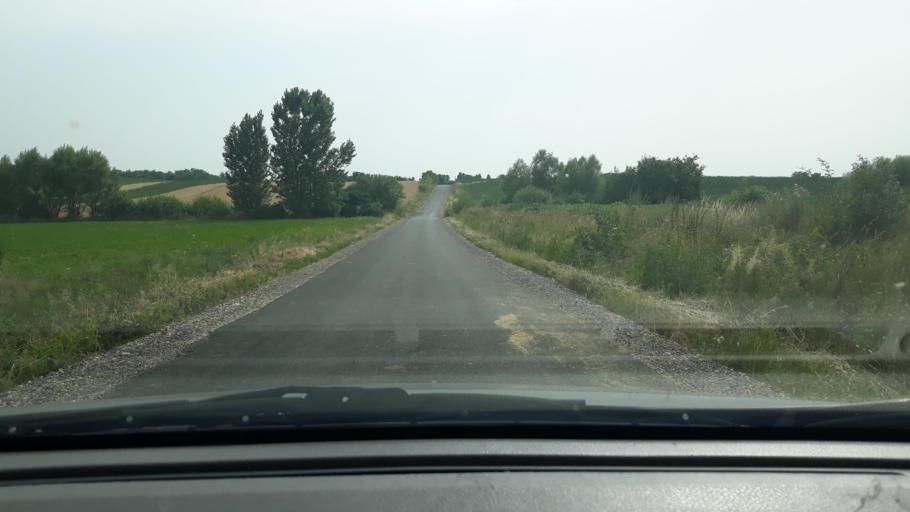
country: RO
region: Bihor
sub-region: Comuna Chislaz
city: Misca
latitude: 47.2701
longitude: 22.2653
